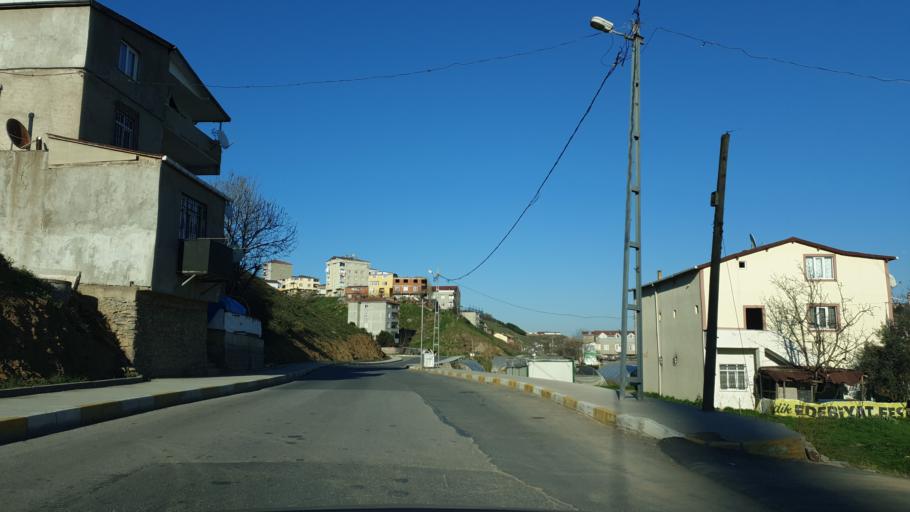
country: TR
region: Istanbul
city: Pendik
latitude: 40.8716
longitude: 29.2852
